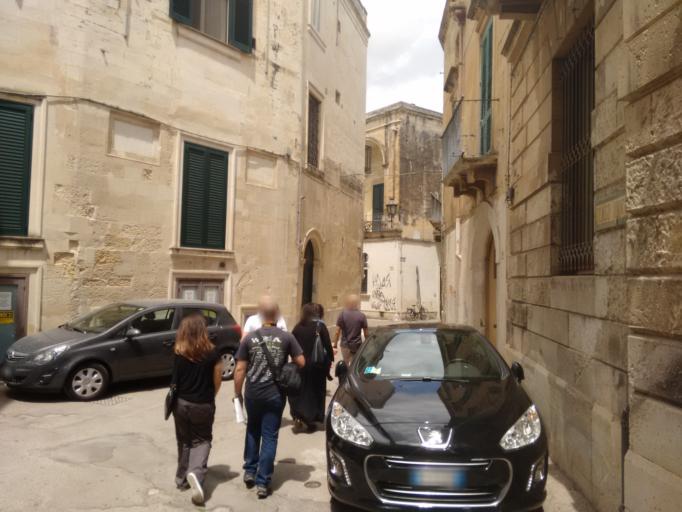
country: IT
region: Apulia
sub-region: Provincia di Lecce
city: Lecce
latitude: 40.3555
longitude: 18.1702
